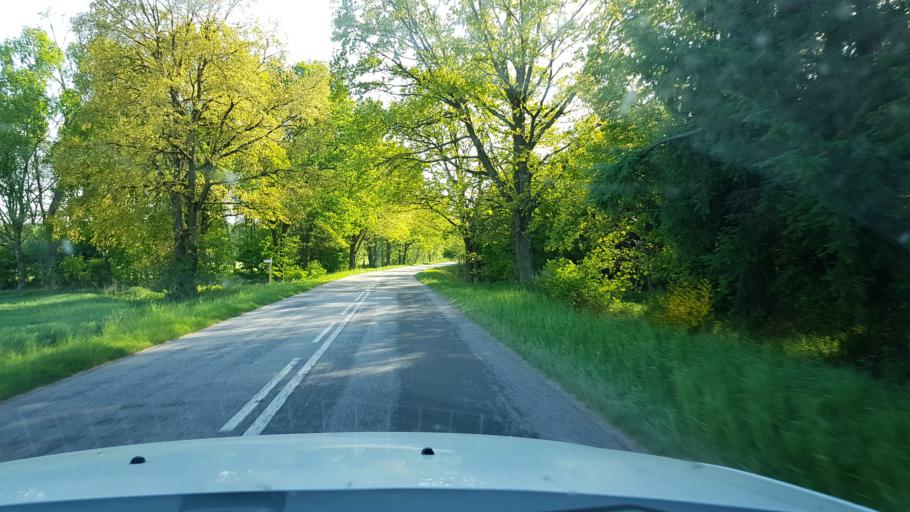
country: PL
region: West Pomeranian Voivodeship
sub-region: Powiat lobeski
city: Resko
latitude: 53.7352
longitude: 15.3554
